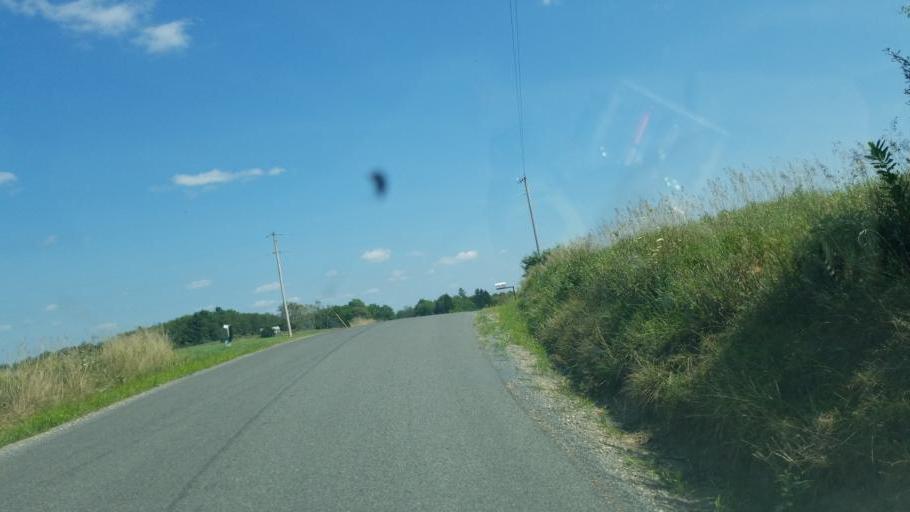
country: US
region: Pennsylvania
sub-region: Clarion County
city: Knox
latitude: 41.0957
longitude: -79.5158
